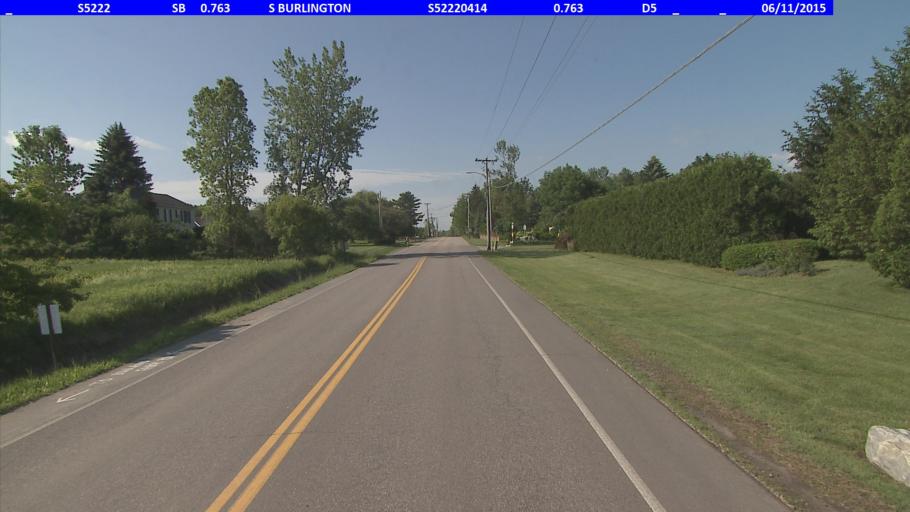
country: US
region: Vermont
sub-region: Chittenden County
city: South Burlington
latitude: 44.4276
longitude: -73.1941
